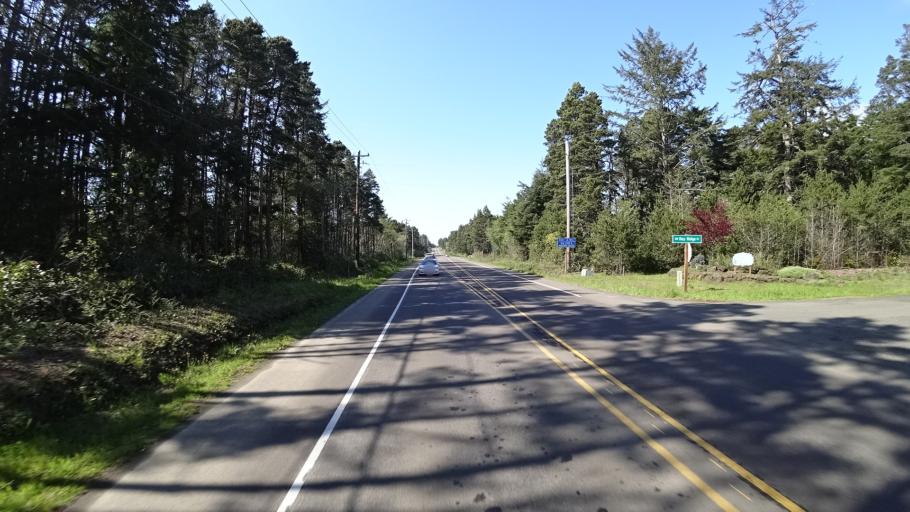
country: US
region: Oregon
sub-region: Lincoln County
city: Waldport
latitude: 44.4628
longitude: -124.0773
